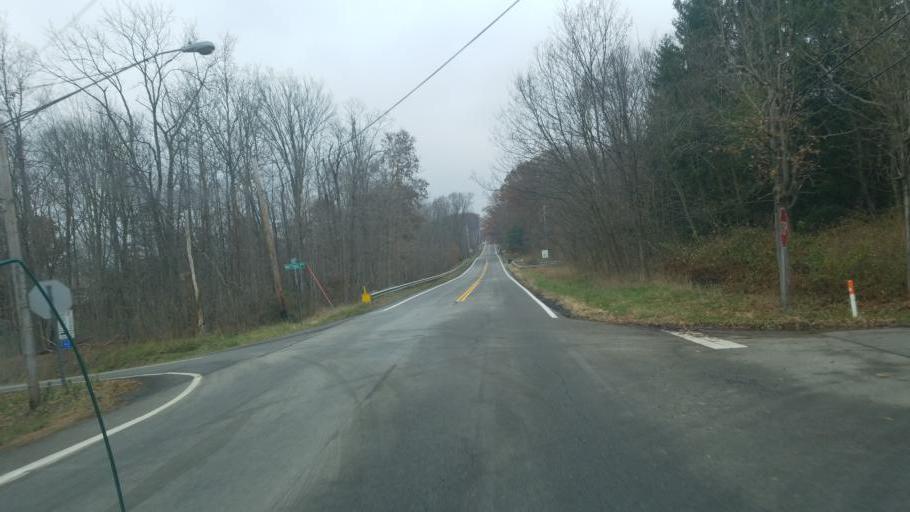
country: US
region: Ohio
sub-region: Cuyahoga County
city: North Royalton
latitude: 41.2587
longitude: -81.7251
